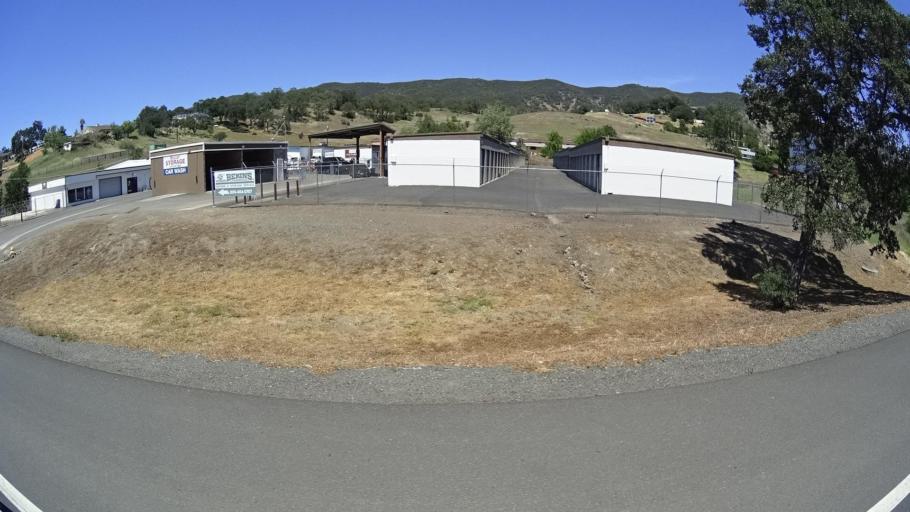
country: US
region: California
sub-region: Lake County
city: Nice
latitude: 39.1269
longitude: -122.8639
